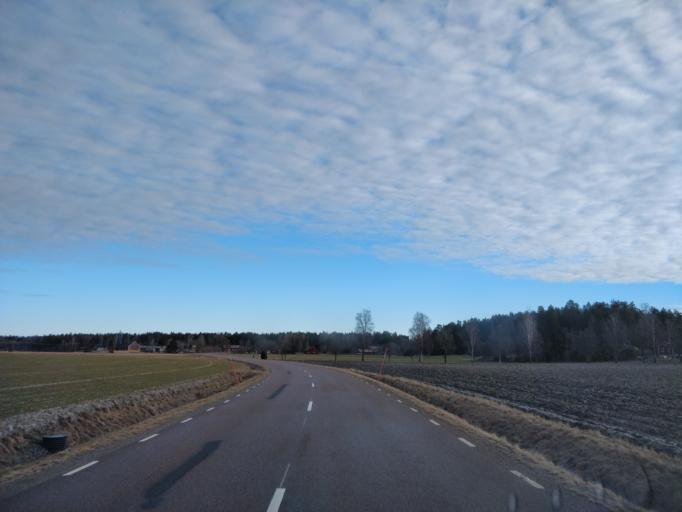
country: SE
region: Uppsala
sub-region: Enkopings Kommun
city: Enkoping
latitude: 59.8074
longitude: 17.1006
